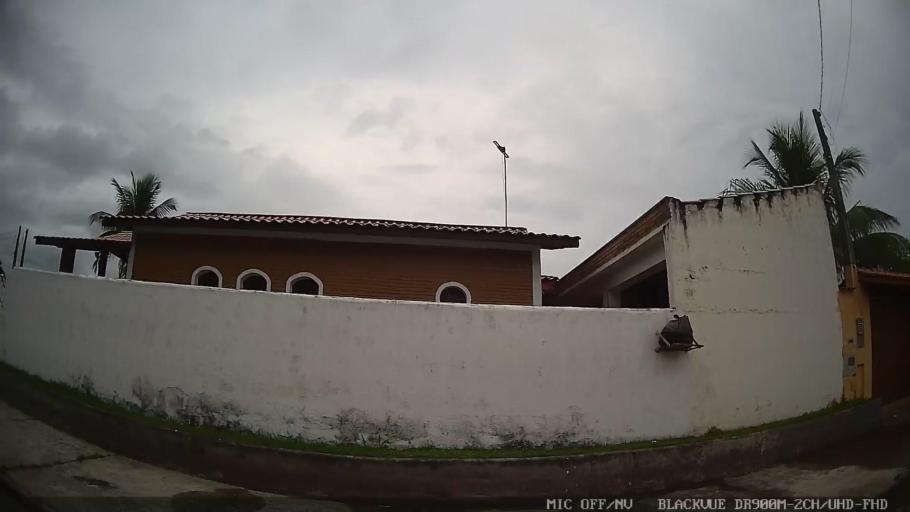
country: BR
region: Sao Paulo
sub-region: Caraguatatuba
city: Caraguatatuba
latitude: -23.6211
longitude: -45.3793
